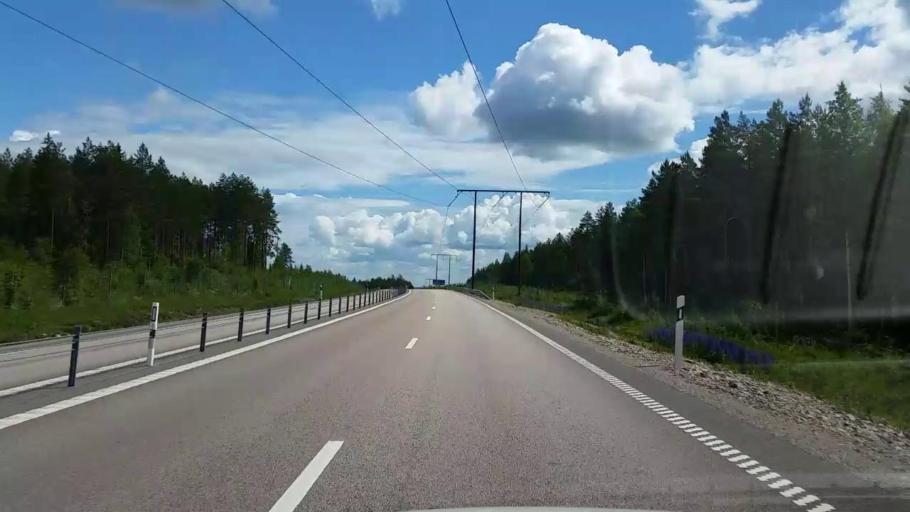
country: SE
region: Dalarna
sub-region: Avesta Kommun
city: Avesta
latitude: 60.1236
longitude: 16.1210
